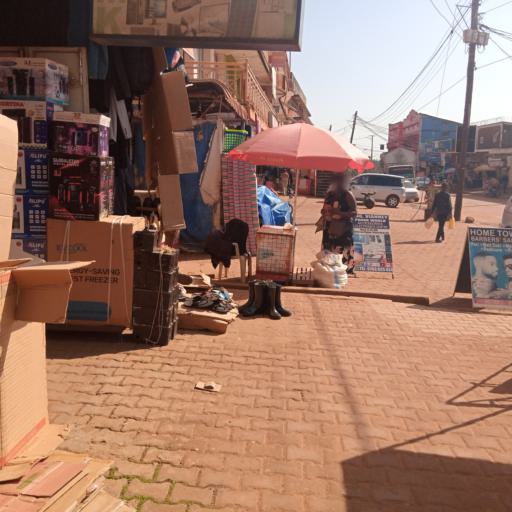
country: UG
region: Central Region
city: Masaka
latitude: -0.3416
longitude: 31.7376
